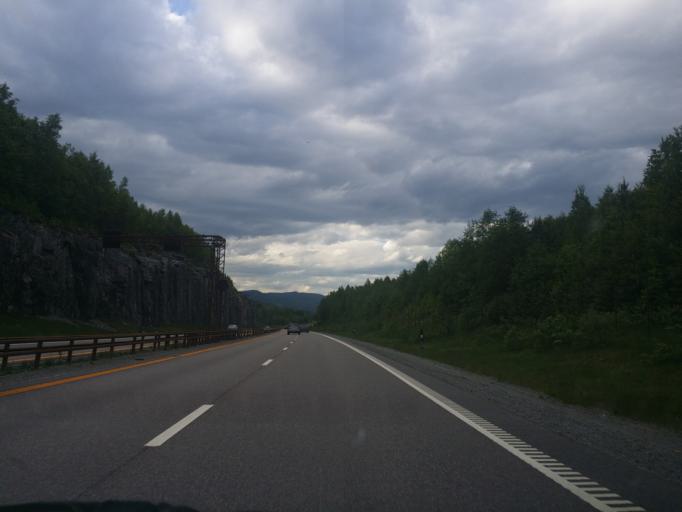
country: NO
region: Akershus
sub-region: Eidsvoll
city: Eidsvoll
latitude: 60.3531
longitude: 11.2080
